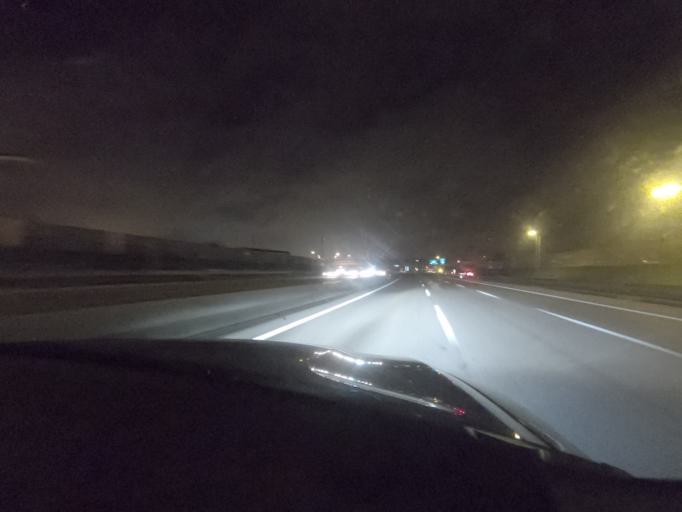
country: PT
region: Lisbon
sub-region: Alenquer
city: Carregado
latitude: 39.0221
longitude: -8.9647
